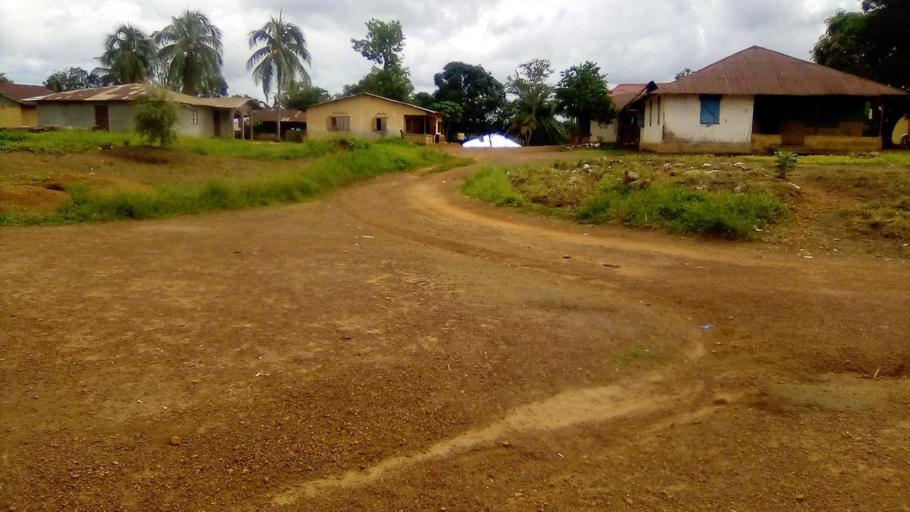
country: SL
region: Southern Province
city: Pujehun
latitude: 7.3609
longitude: -11.7255
